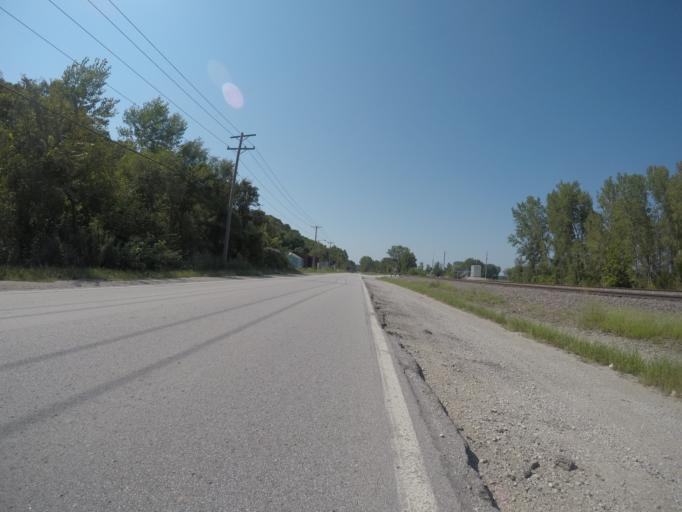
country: US
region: Kansas
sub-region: Leavenworth County
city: Lansing
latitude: 39.1900
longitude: -94.8032
